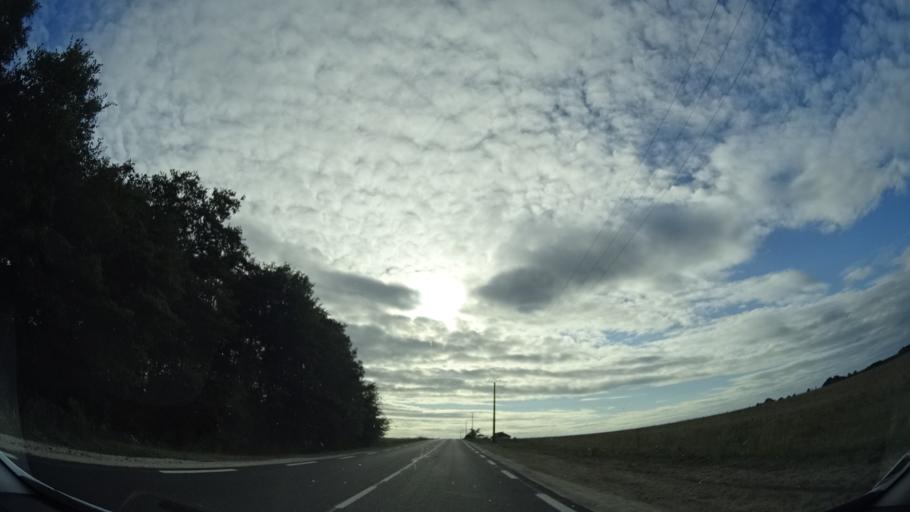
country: FR
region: Centre
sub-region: Departement du Loir-et-Cher
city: La Ville-aux-Clercs
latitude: 47.8927
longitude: 1.0973
